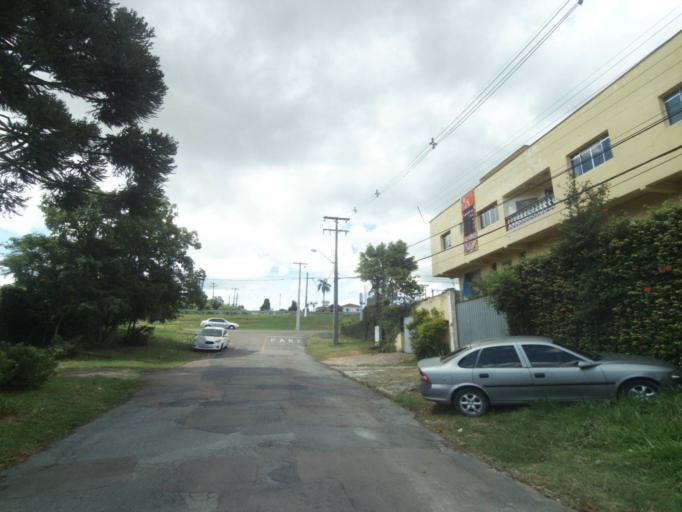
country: BR
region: Parana
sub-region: Curitiba
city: Curitiba
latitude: -25.4314
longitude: -49.3309
